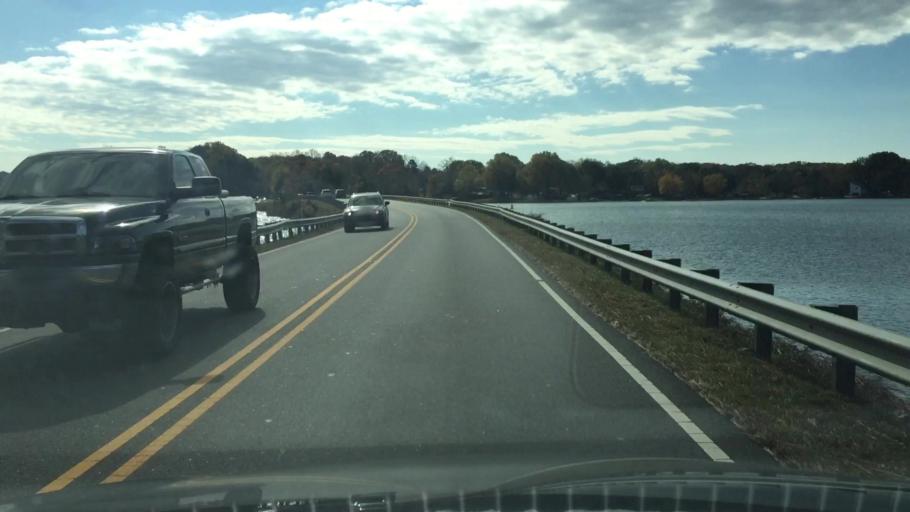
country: US
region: North Carolina
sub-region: Iredell County
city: Mooresville
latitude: 35.5661
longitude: -80.8662
